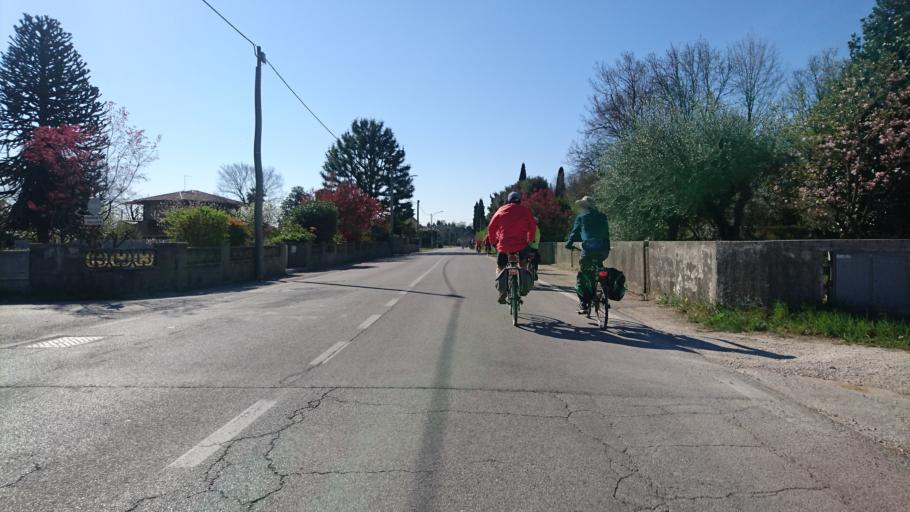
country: IT
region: Veneto
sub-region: Provincia di Vicenza
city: Rosa
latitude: 45.7292
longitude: 11.7438
